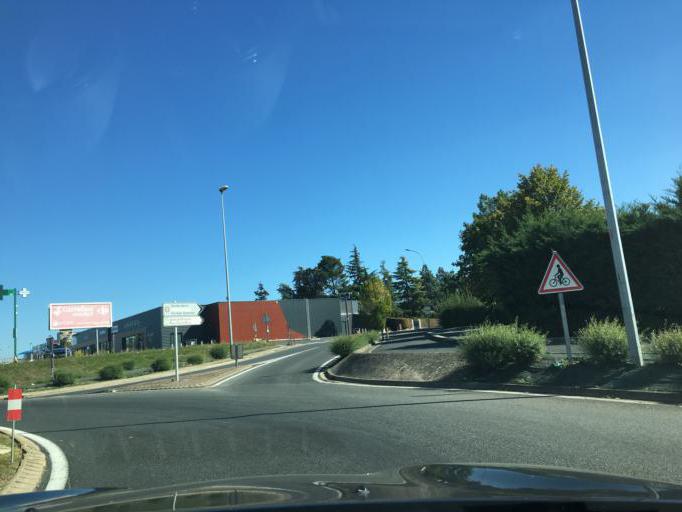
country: FR
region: Centre
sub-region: Departement d'Indre-et-Loire
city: Azay-le-Rideau
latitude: 47.2667
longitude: 0.4718
